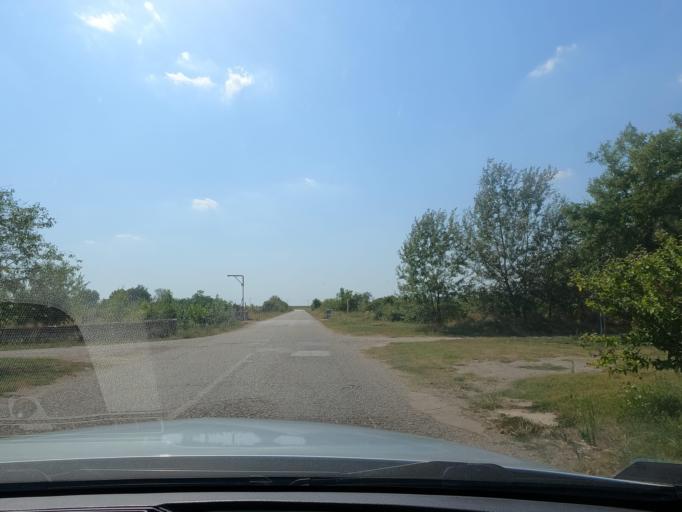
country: RS
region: Autonomna Pokrajina Vojvodina
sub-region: Severnobacki Okrug
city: Subotica
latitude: 46.0621
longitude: 19.7527
